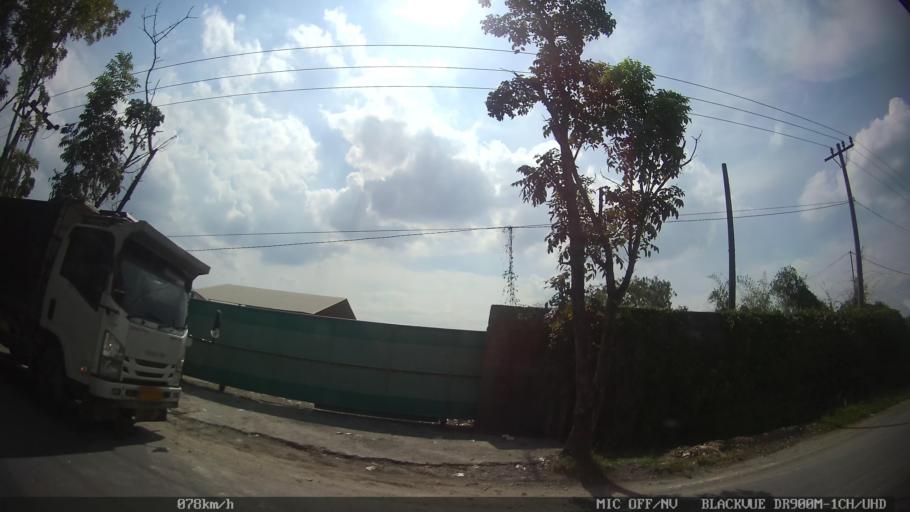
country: ID
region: North Sumatra
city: Binjai
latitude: 3.6238
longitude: 98.5347
